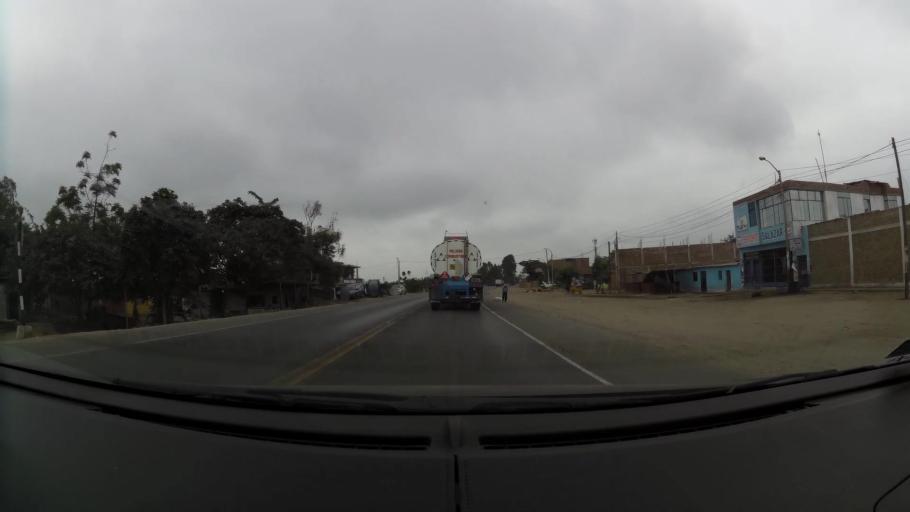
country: PE
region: La Libertad
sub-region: Viru
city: Viru
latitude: -8.4306
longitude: -78.7762
